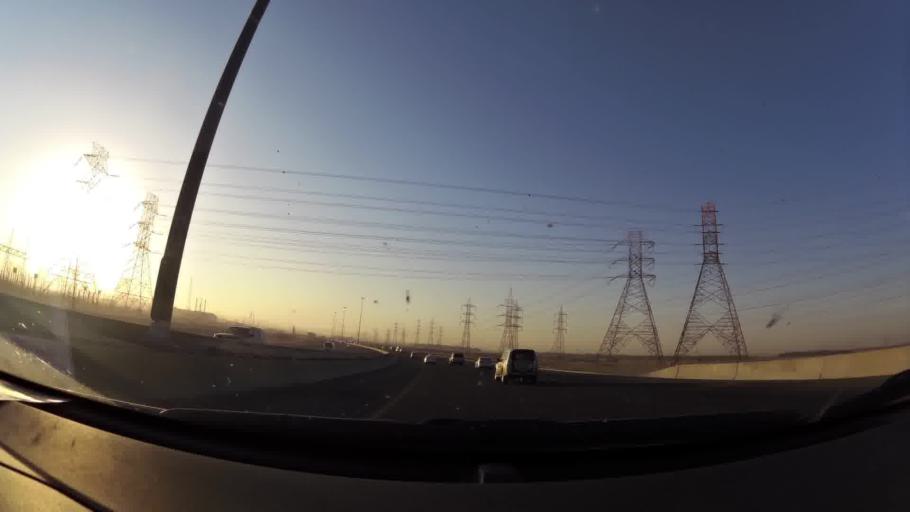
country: KW
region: Al Ahmadi
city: Al Ahmadi
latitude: 29.0583
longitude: 48.1084
